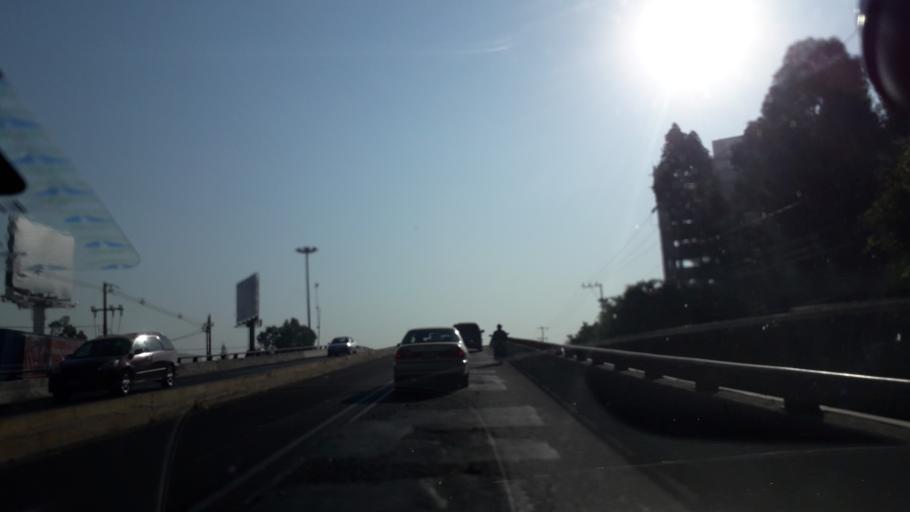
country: MX
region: Puebla
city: Tlazcalancingo
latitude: 19.0376
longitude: -98.2463
